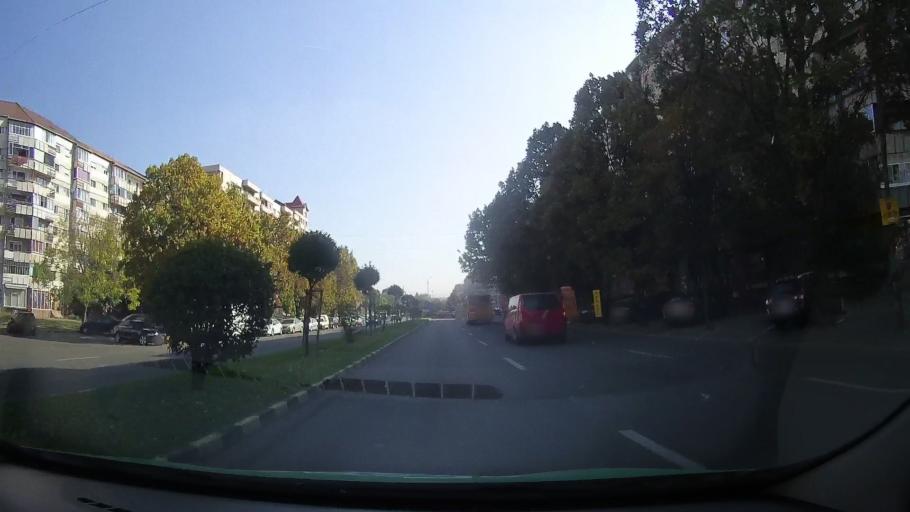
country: RO
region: Bihor
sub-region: Comuna Biharea
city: Oradea
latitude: 47.0702
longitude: 21.9222
